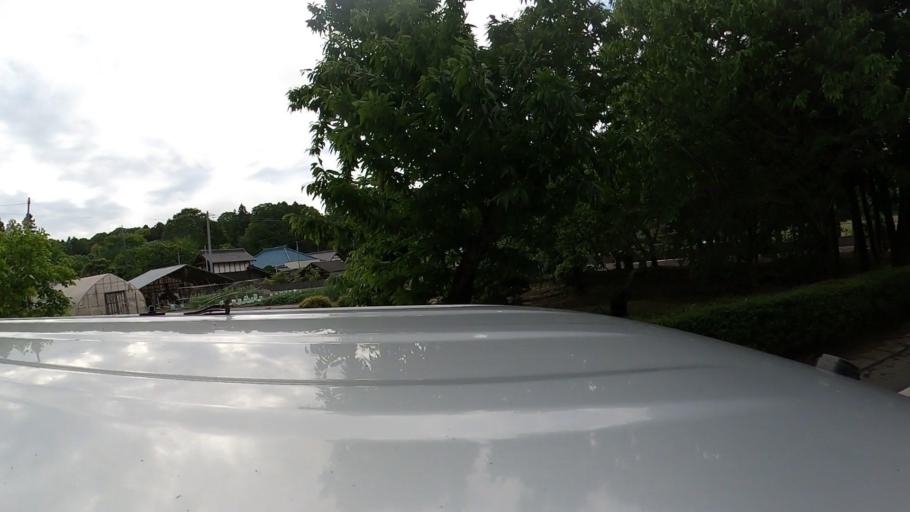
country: JP
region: Ibaraki
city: Ami
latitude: 35.9770
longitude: 140.2366
